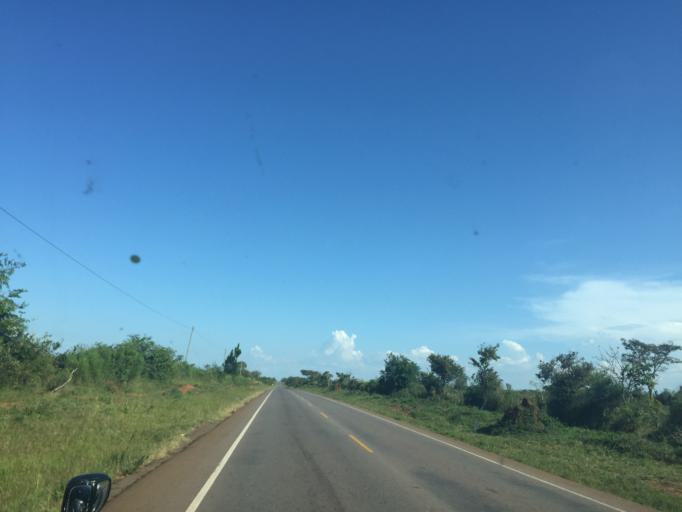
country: UG
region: Central Region
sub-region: Nakasongola District
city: Nakasongola
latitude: 1.3691
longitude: 32.3557
